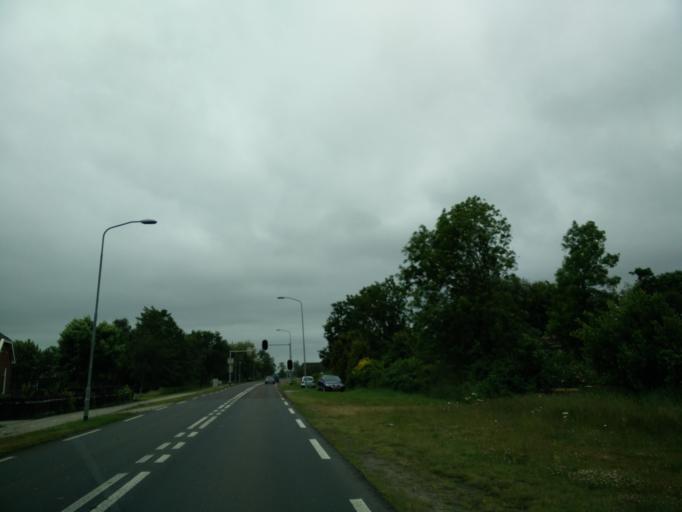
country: NL
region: Groningen
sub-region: Gemeente Groningen
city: Groningen
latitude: 53.1882
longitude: 6.5113
